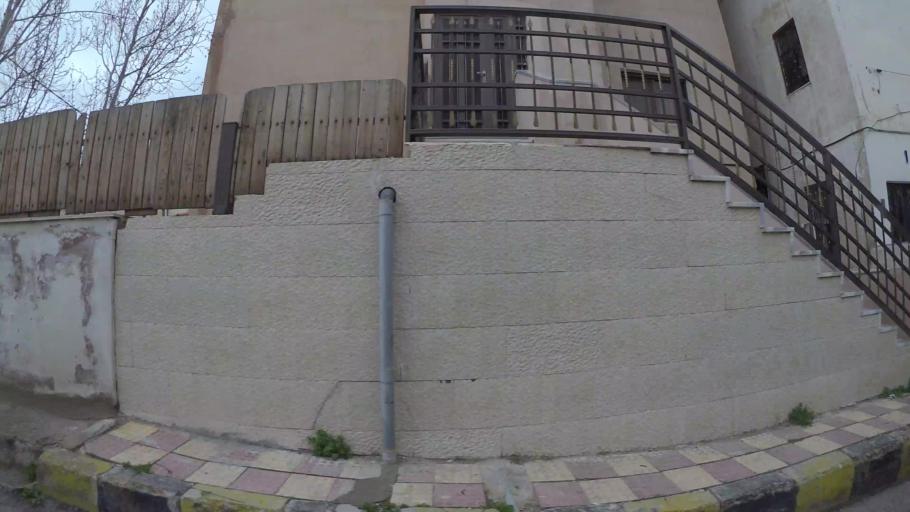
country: JO
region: Amman
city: Wadi as Sir
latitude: 31.9476
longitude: 35.8150
